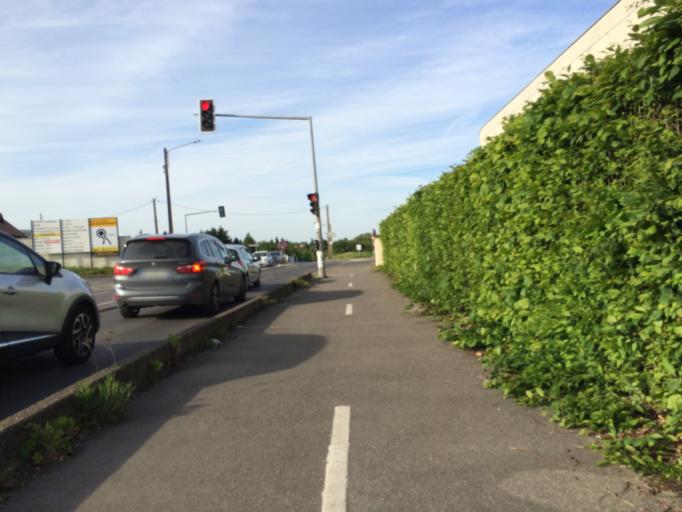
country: FR
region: Ile-de-France
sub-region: Departement de l'Essonne
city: Montlhery
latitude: 48.6487
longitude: 2.2759
